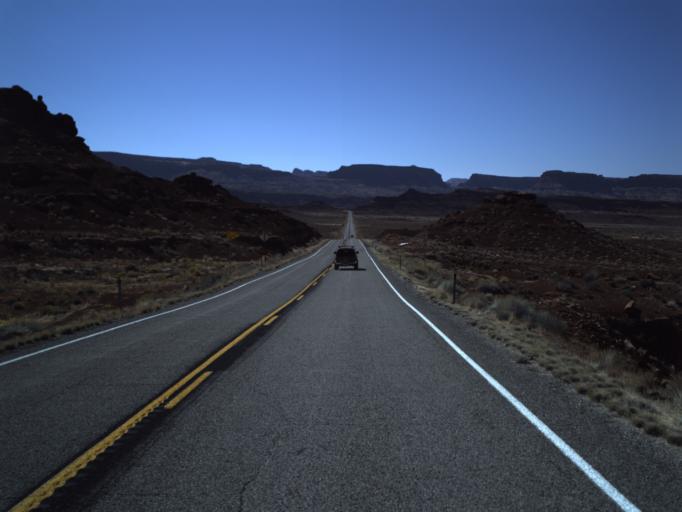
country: US
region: Utah
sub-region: San Juan County
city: Blanding
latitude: 37.8536
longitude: -110.3533
